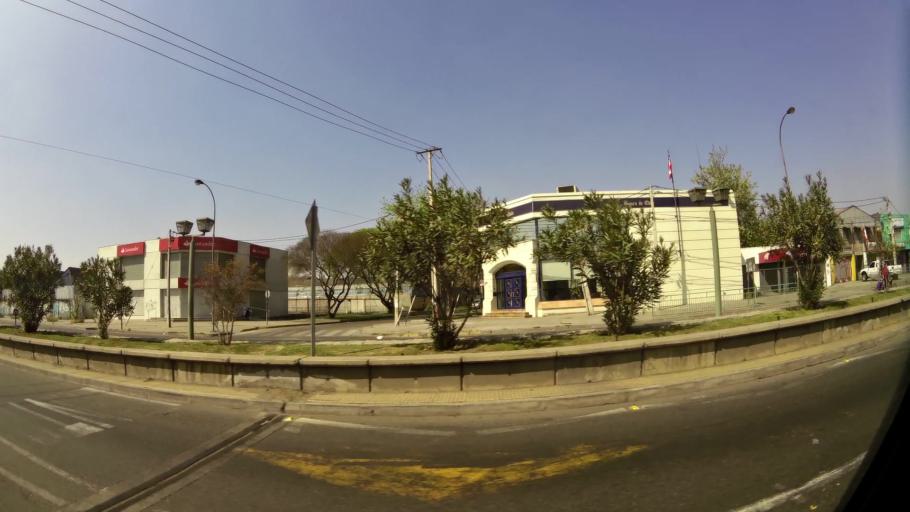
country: CL
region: Santiago Metropolitan
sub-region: Provincia de Santiago
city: Lo Prado
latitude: -33.4305
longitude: -70.6923
